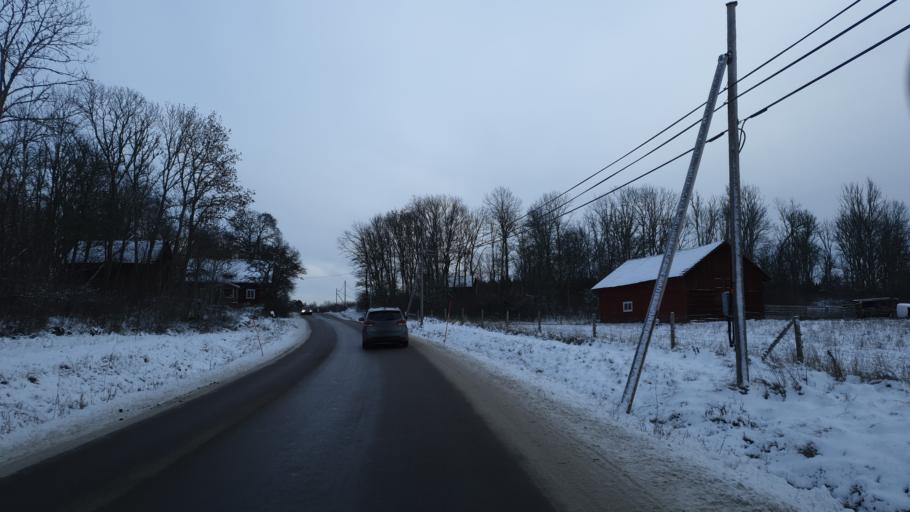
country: SE
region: Uppsala
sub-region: Uppsala Kommun
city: Saevja
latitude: 59.7073
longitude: 17.5950
